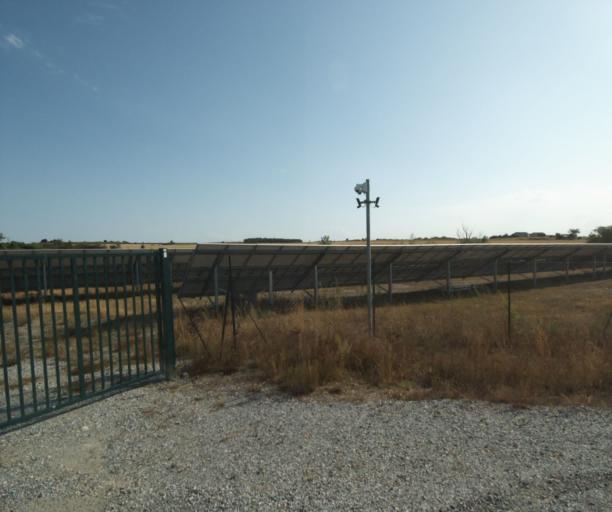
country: FR
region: Midi-Pyrenees
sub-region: Departement de la Haute-Garonne
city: Avignonet-Lauragais
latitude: 43.4407
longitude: 1.8131
